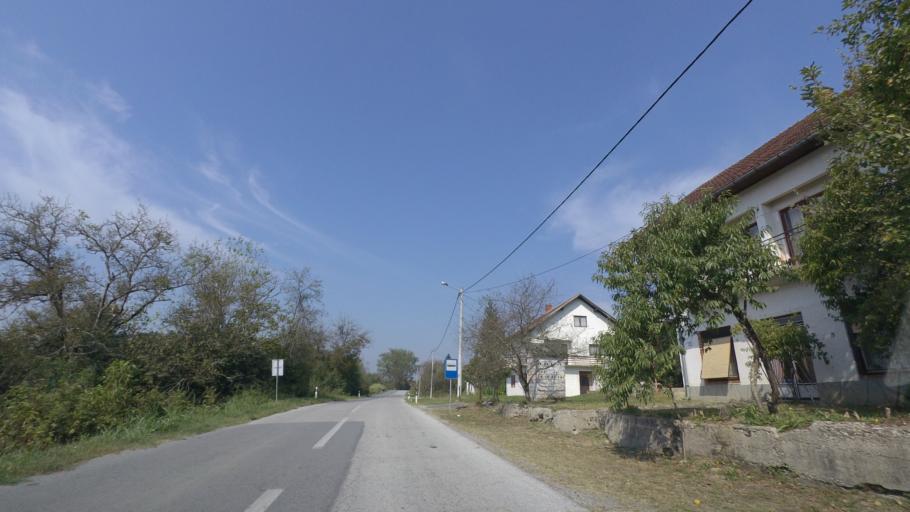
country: BA
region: Republika Srpska
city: Knezica
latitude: 45.2043
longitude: 16.6890
